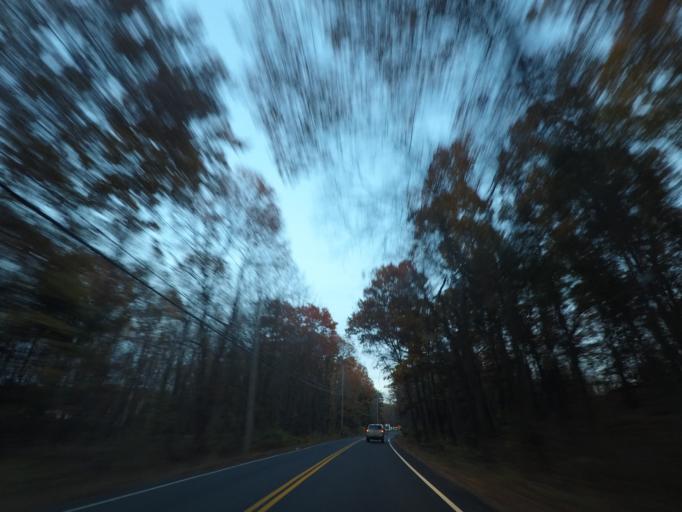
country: US
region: New York
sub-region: Albany County
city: Westmere
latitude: 42.7451
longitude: -73.9055
